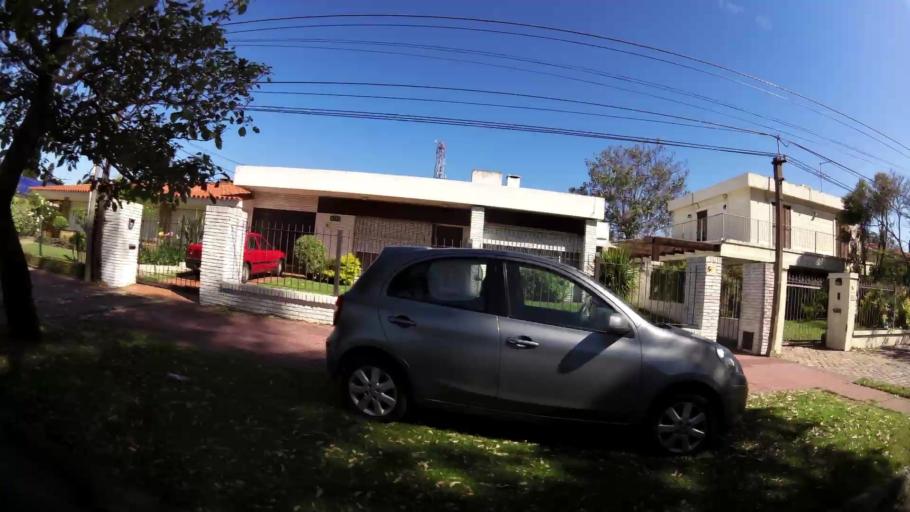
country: UY
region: Canelones
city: Paso de Carrasco
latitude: -34.8901
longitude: -56.0697
